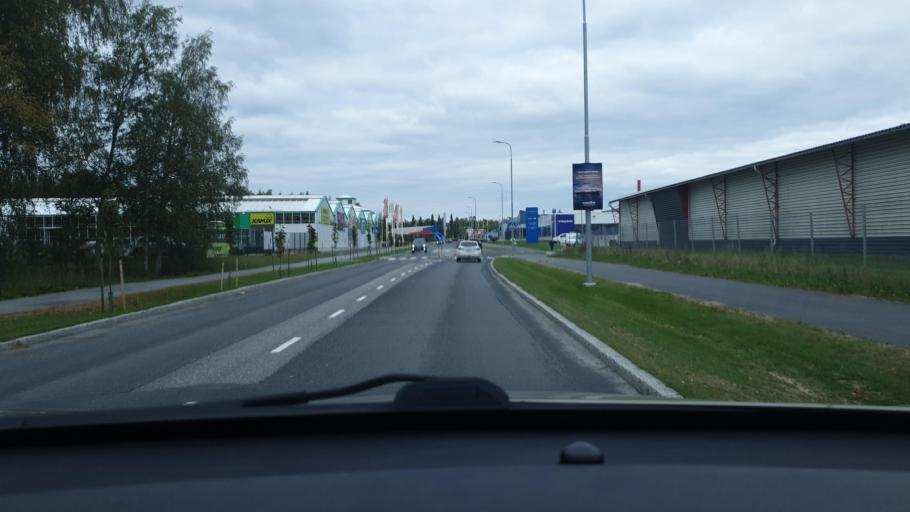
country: FI
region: Ostrobothnia
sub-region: Vaasa
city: Vaasa
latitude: 63.1062
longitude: 21.6472
